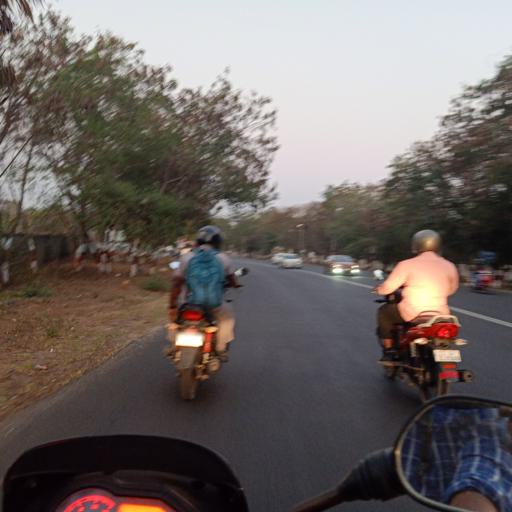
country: IN
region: Telangana
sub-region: Rangareddi
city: Secunderabad
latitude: 17.5429
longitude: 78.5320
